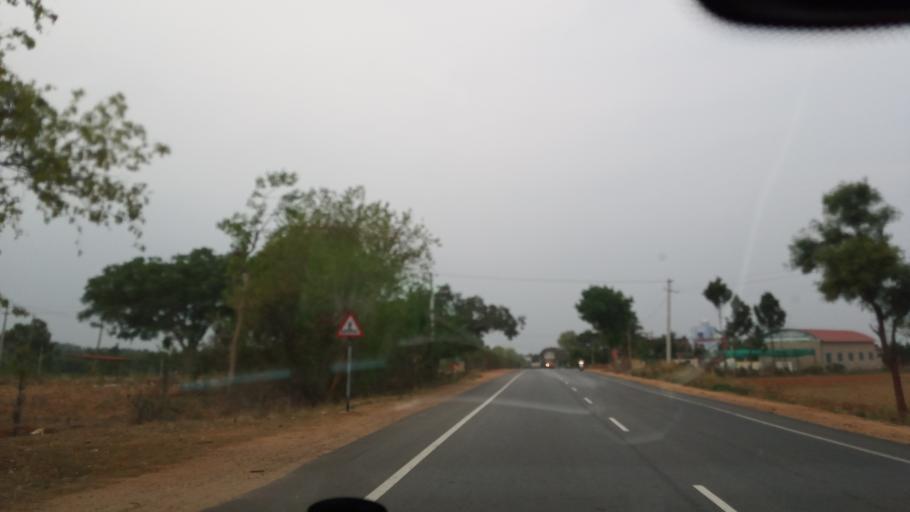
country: IN
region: Karnataka
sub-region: Mandya
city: Nagamangala
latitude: 12.7808
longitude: 76.7444
